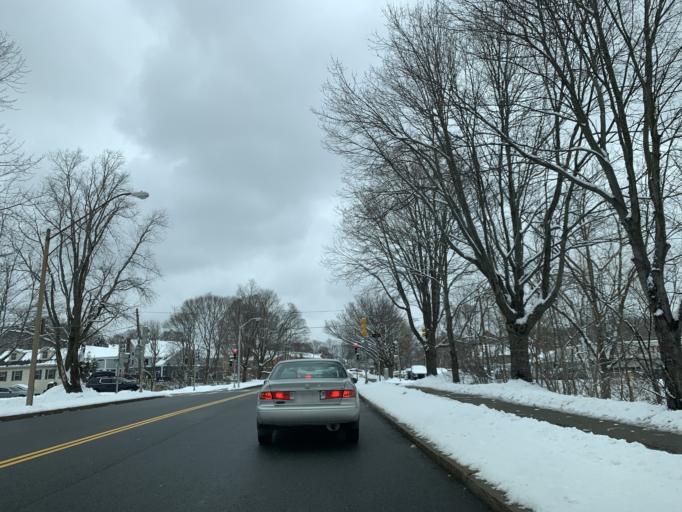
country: US
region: Massachusetts
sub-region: Suffolk County
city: Jamaica Plain
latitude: 42.2856
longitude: -71.1477
